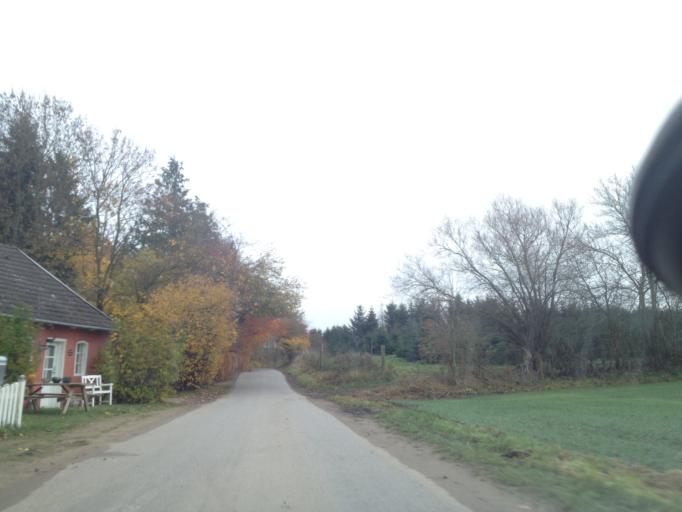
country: DK
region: South Denmark
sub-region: Assens Kommune
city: Vissenbjerg
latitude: 55.4280
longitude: 10.1835
